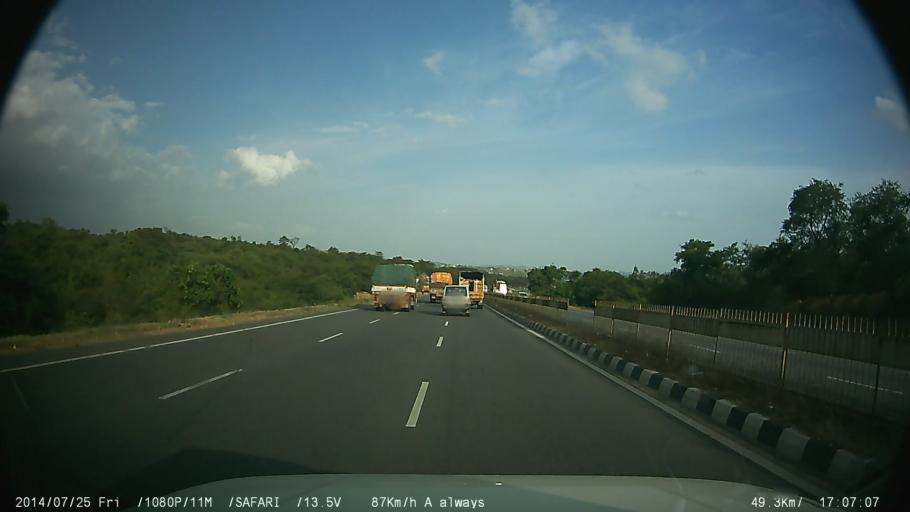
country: IN
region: Tamil Nadu
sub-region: Krishnagiri
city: Hosur
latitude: 12.6983
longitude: 77.9126
